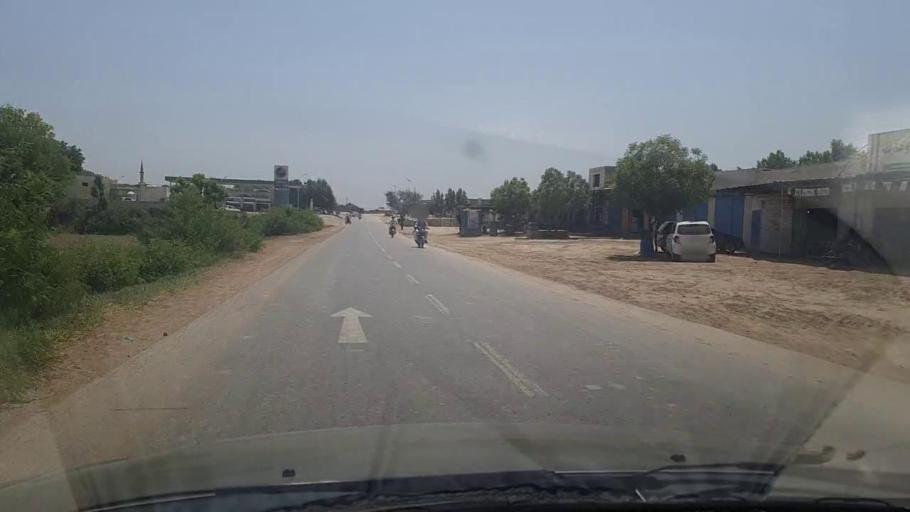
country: PK
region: Sindh
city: Tando Jam
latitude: 25.3113
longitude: 68.5696
